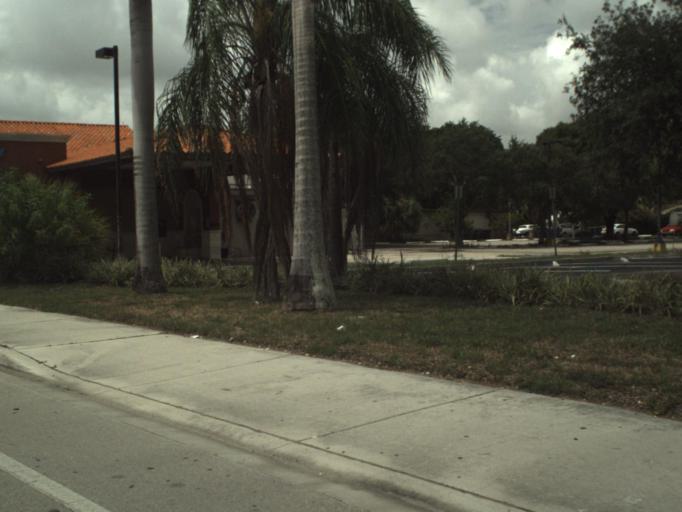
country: US
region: Florida
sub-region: Broward County
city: Hallandale Beach
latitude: 25.9843
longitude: -80.1425
